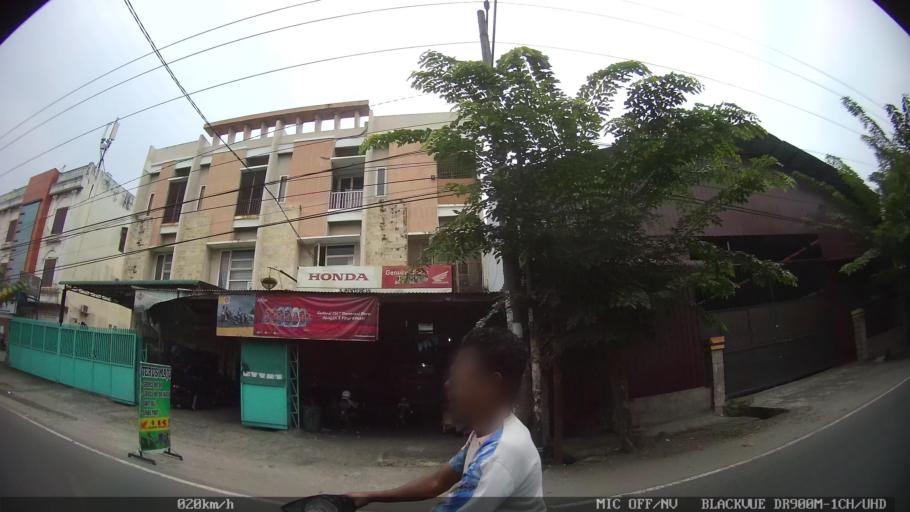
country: ID
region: North Sumatra
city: Medan
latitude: 3.5604
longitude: 98.7208
